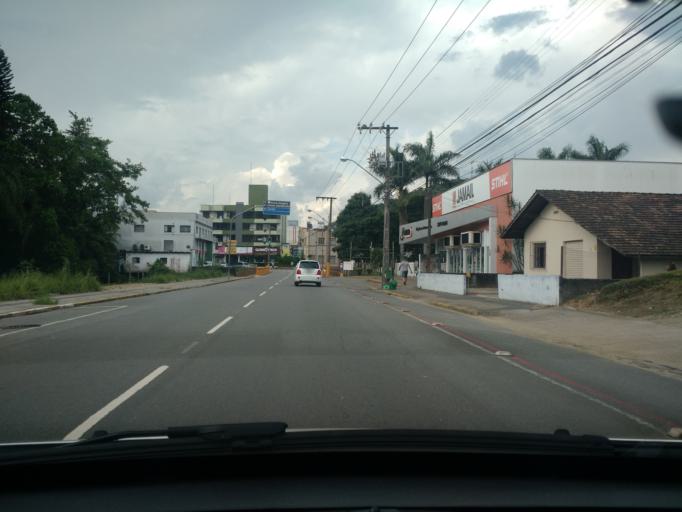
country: BR
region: Santa Catarina
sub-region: Jaragua Do Sul
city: Jaragua do Sul
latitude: -26.4964
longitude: -49.0878
